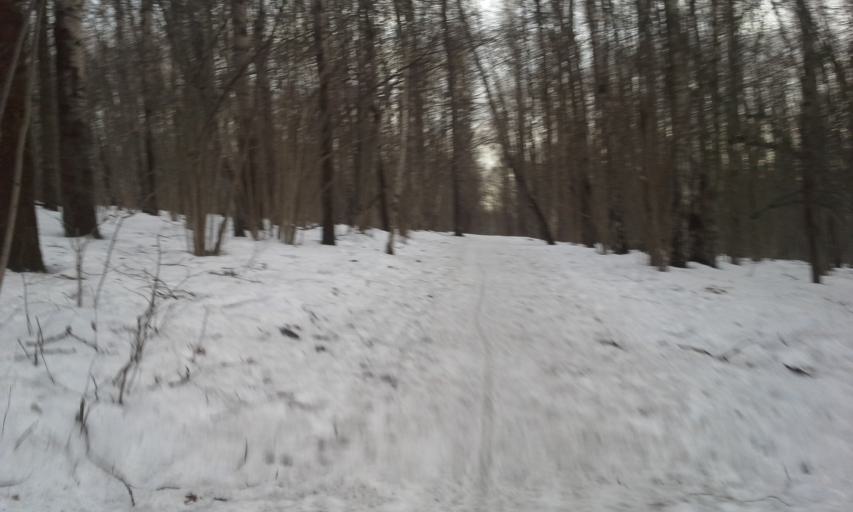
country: RU
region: Moscow
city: Zyuzino
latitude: 55.6367
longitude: 37.5773
